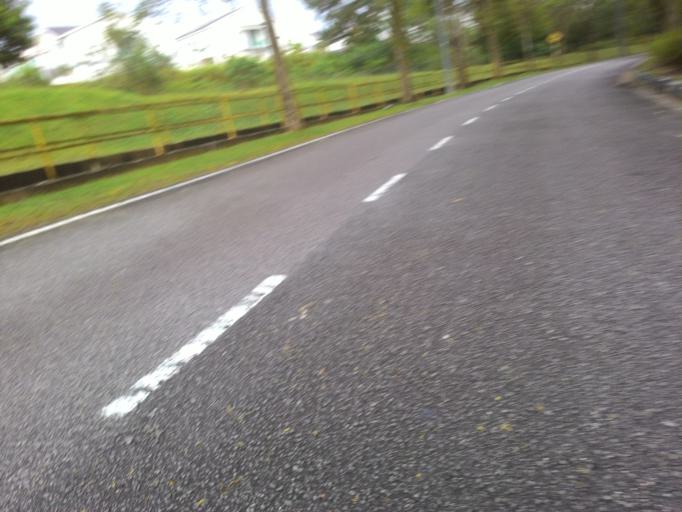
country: MY
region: Kedah
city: Kulim
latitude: 5.3833
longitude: 100.5803
